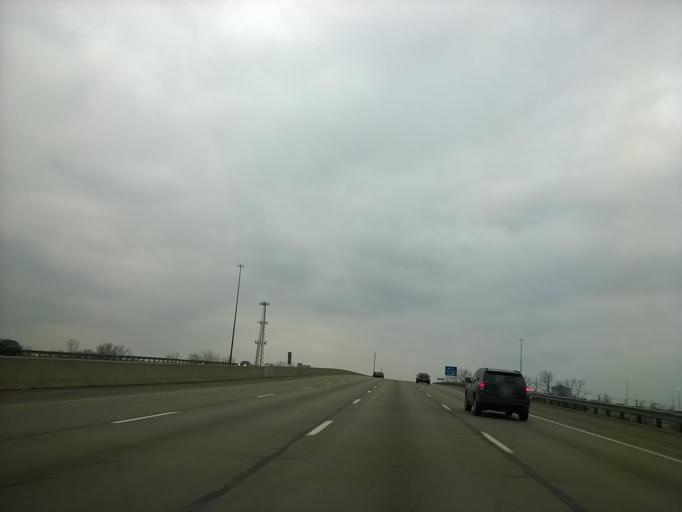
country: US
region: Indiana
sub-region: Marion County
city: Warren Park
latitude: 39.7988
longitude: -86.0986
